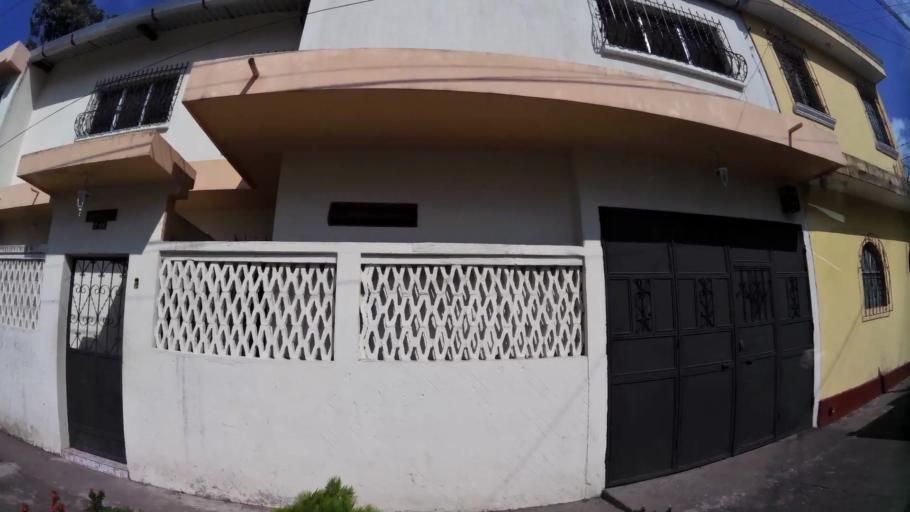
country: GT
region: Retalhuleu
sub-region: Municipio de Retalhuleu
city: Retalhuleu
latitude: 14.5440
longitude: -91.6807
